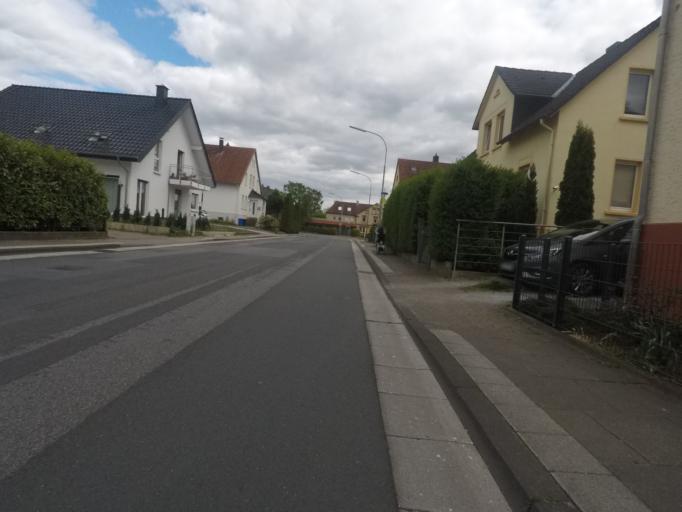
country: DE
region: North Rhine-Westphalia
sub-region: Regierungsbezirk Detmold
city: Herford
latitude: 52.1130
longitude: 8.6936
